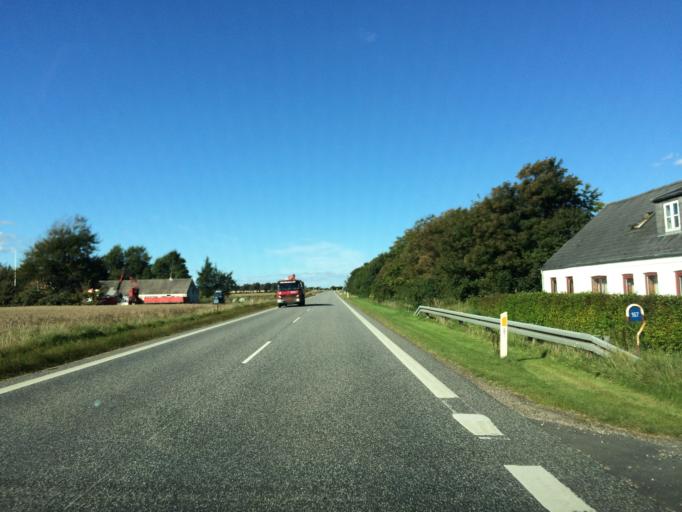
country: DK
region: Central Jutland
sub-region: Holstebro Kommune
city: Holstebro
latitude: 56.3053
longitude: 8.6036
